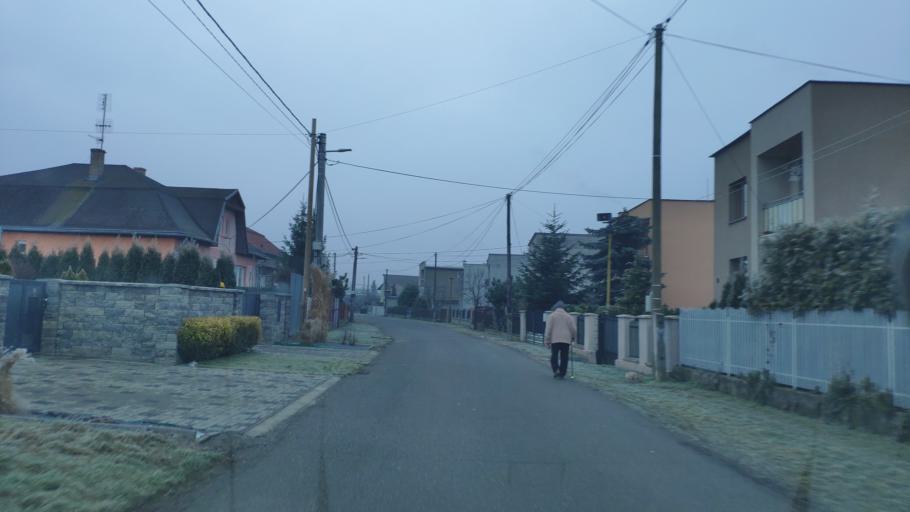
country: SK
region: Kosicky
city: Kosice
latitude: 48.6163
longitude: 21.3196
